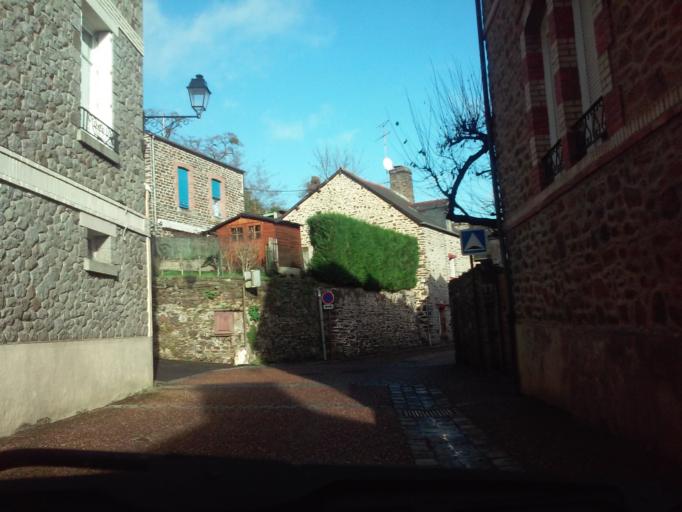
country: FR
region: Brittany
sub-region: Departement d'Ille-et-Vilaine
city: Fougeres
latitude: 48.3517
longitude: -1.2090
